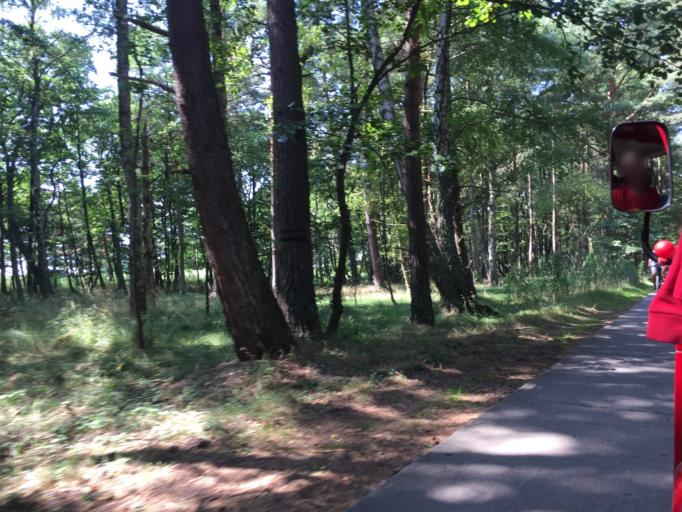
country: PL
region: Pomeranian Voivodeship
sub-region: Powiat leborski
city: Leba
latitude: 54.7539
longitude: 17.5065
